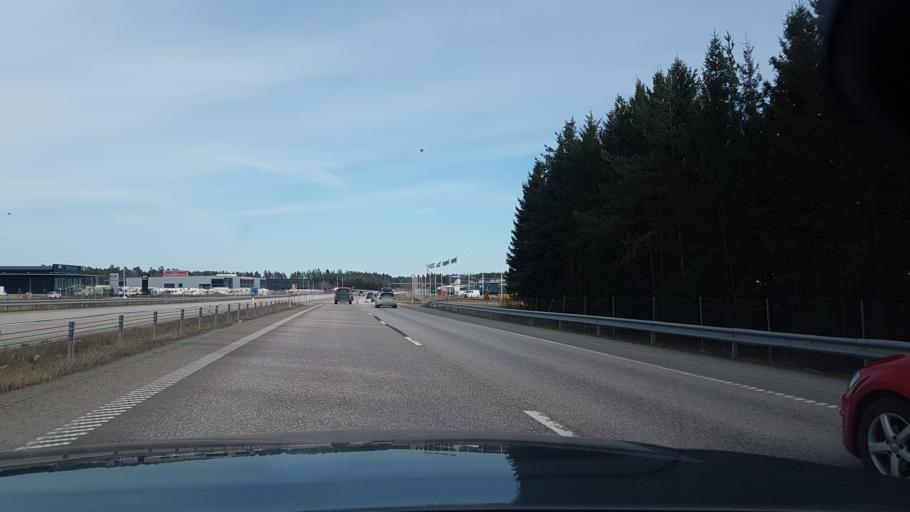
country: SE
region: Uppsala
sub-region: Enkopings Kommun
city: Enkoping
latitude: 59.6502
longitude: 17.1316
